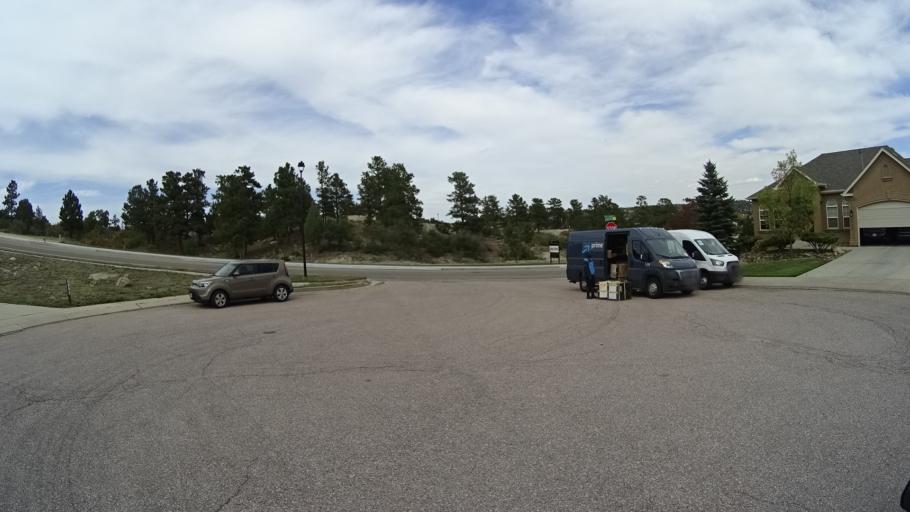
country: US
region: Colorado
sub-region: El Paso County
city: Colorado Springs
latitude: 38.9018
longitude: -104.7894
